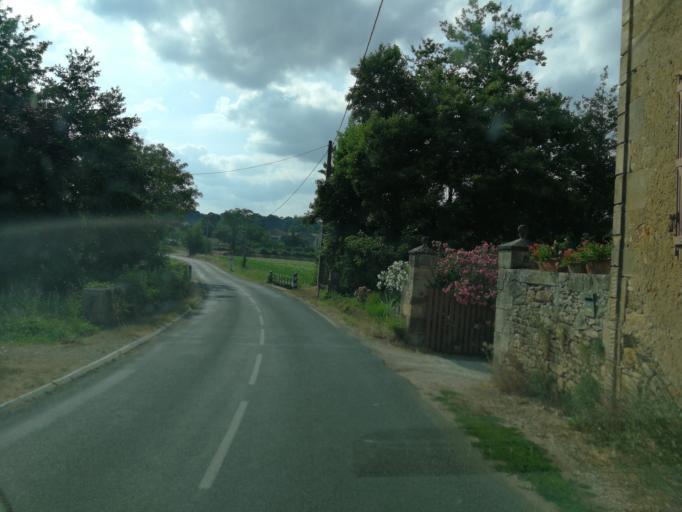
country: FR
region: Aquitaine
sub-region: Departement du Lot-et-Garonne
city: Fumel
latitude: 44.5268
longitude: 0.9437
